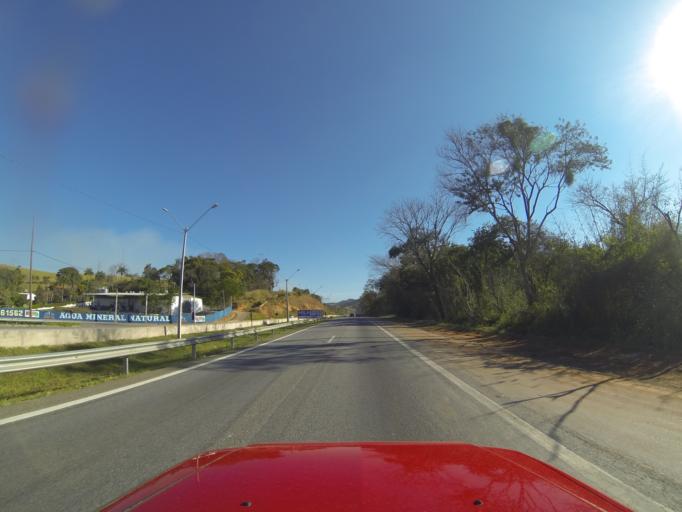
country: BR
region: Sao Paulo
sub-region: Atibaia
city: Atibaia
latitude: -23.0477
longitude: -46.5638
